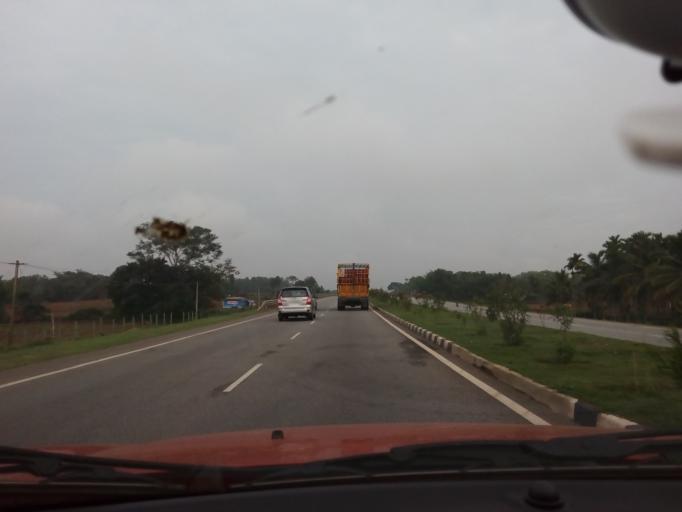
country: IN
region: Karnataka
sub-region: Tumkur
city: Kunigal
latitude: 13.0205
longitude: 77.0611
